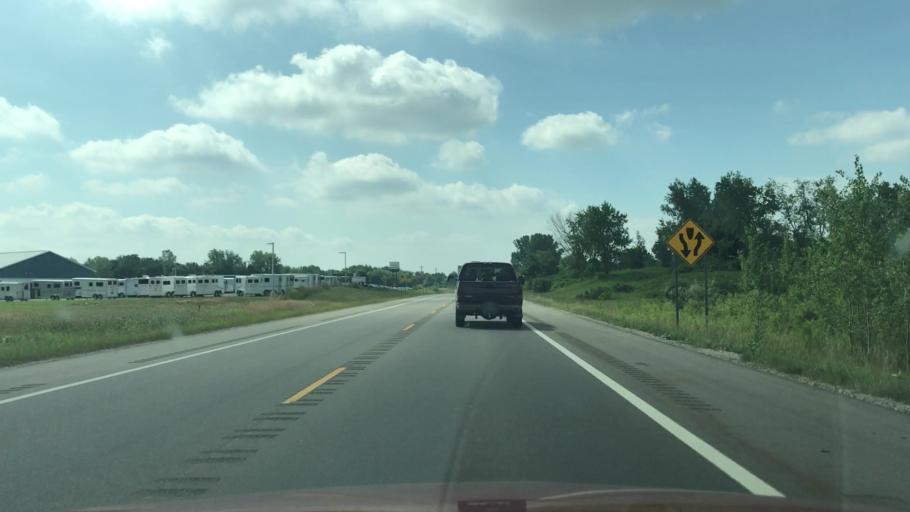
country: US
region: Michigan
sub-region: Kent County
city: Sparta
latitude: 43.1299
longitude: -85.7133
